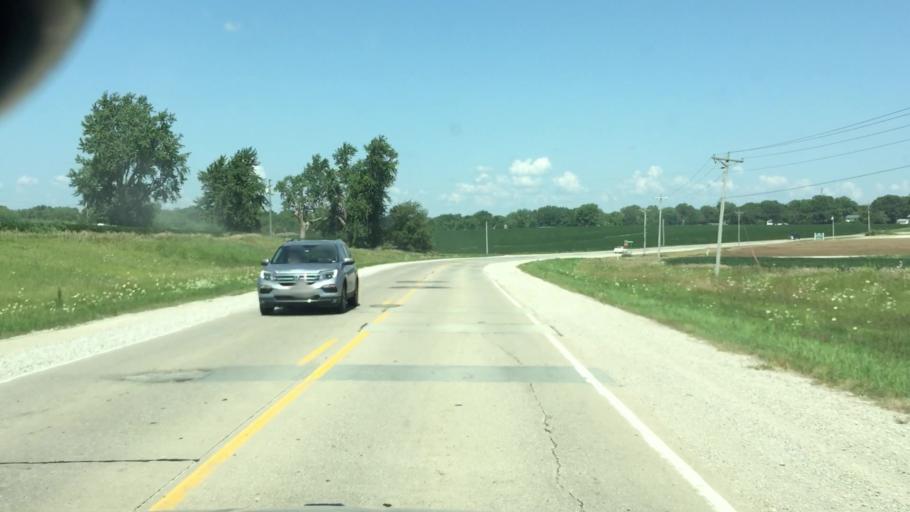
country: US
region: Iowa
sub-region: Jasper County
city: Newton
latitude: 41.6908
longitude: -93.0129
